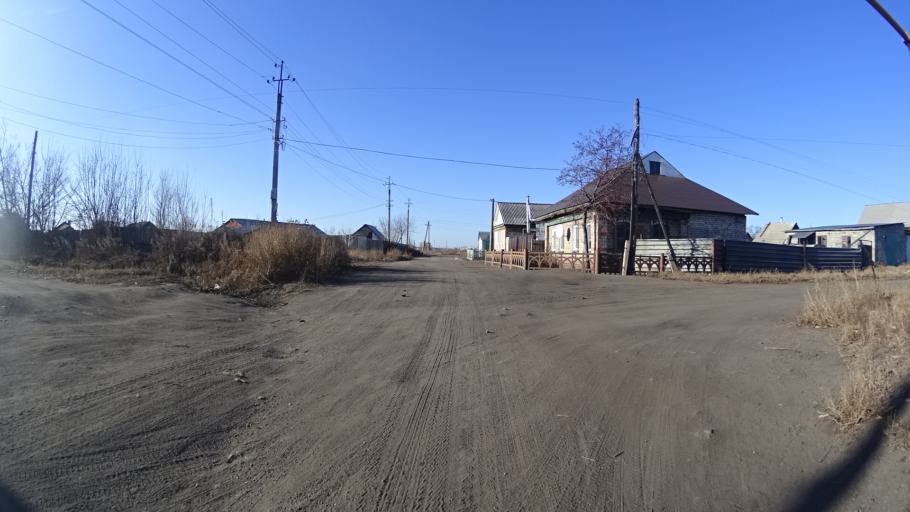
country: RU
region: Chelyabinsk
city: Troitsk
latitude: 54.0933
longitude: 61.5836
